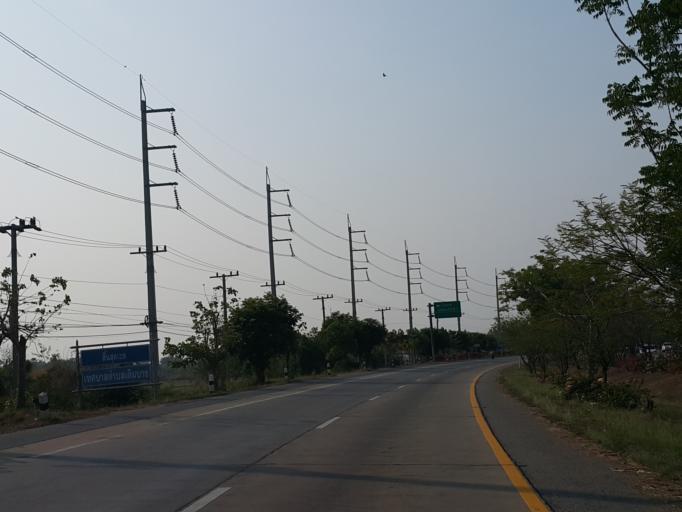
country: TH
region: Suphan Buri
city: Doem Bang Nang Buat
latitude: 14.9089
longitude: 100.0831
